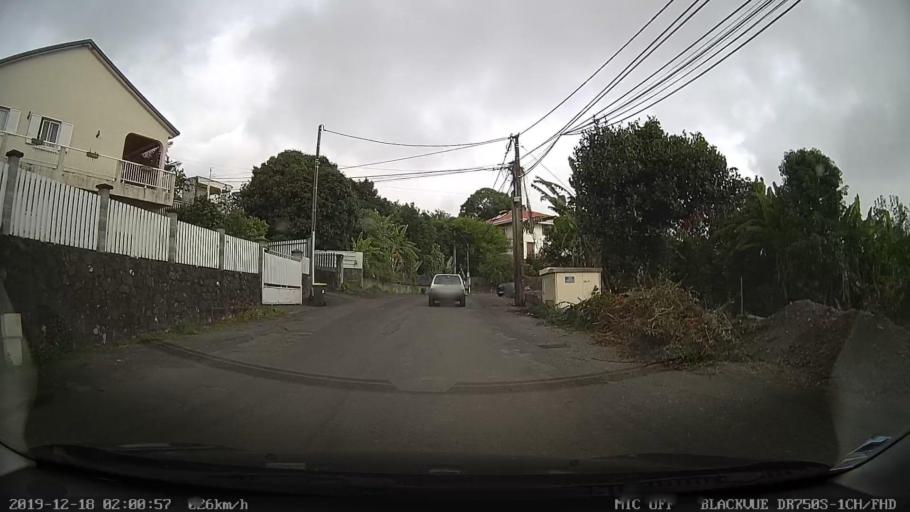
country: RE
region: Reunion
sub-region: Reunion
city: Le Tampon
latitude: -21.2526
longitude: 55.5195
